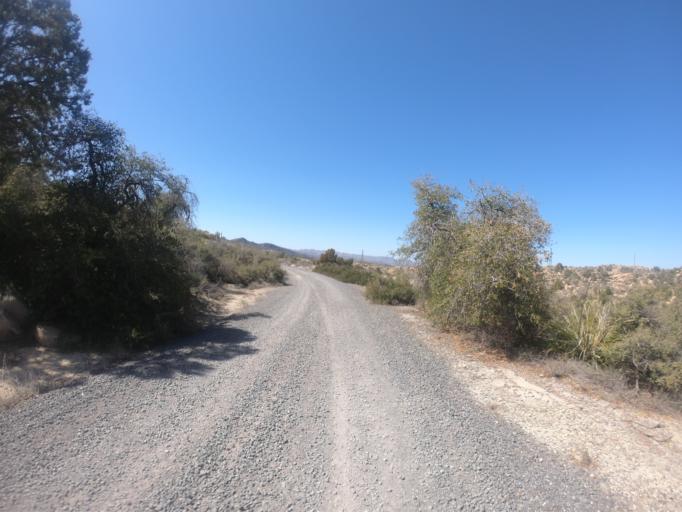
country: US
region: Arizona
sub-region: Gila County
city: Miami
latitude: 33.3569
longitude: -110.9706
